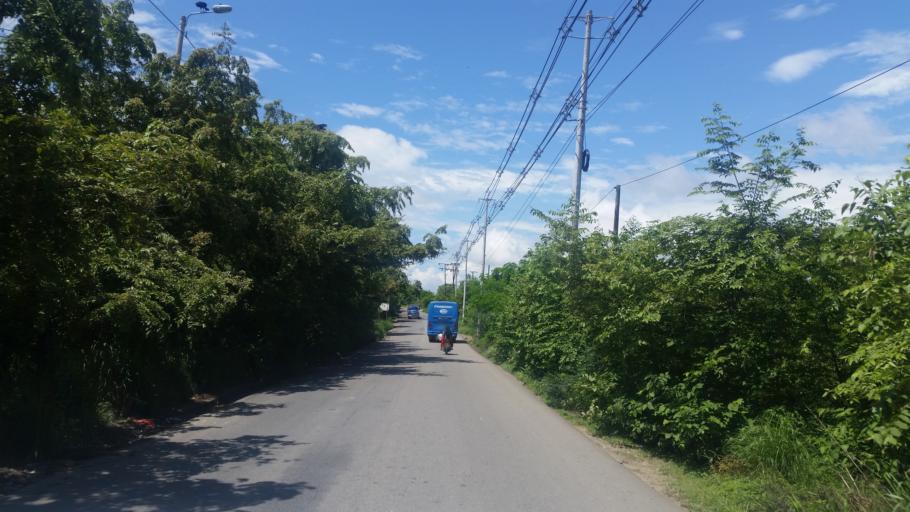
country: CO
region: Huila
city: Neiva
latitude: 2.9833
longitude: -75.2813
